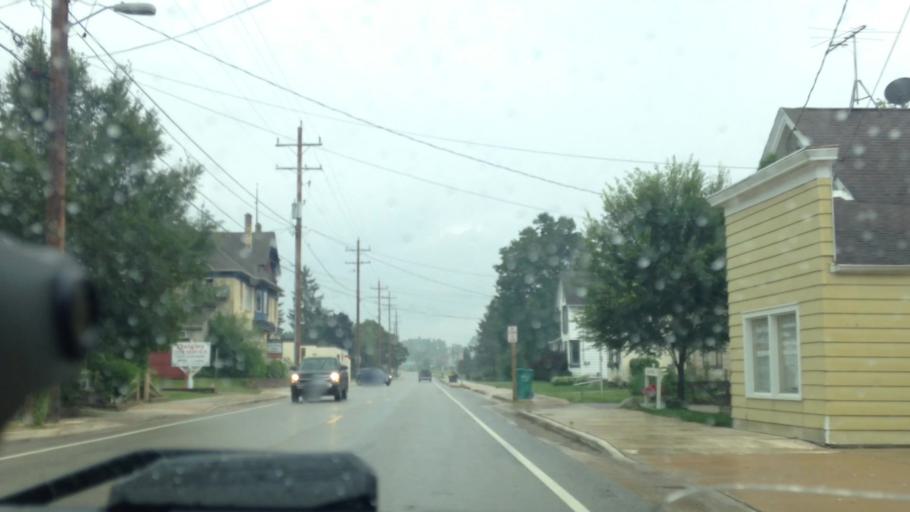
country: US
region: Wisconsin
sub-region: Washington County
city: Richfield
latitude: 43.2570
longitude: -88.1948
